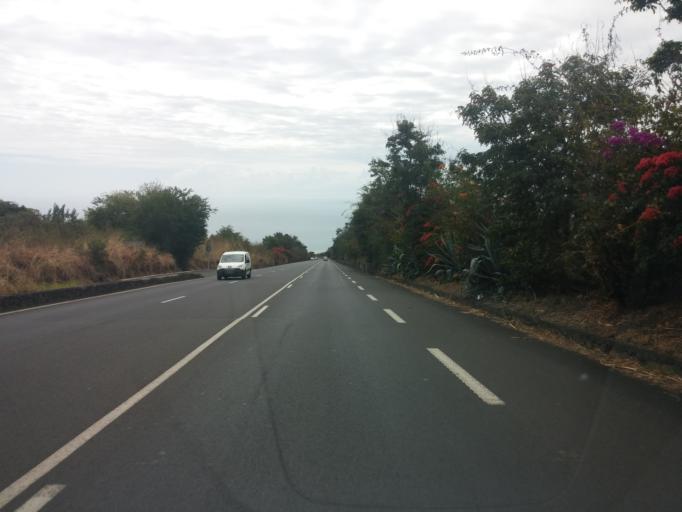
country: RE
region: Reunion
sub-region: Reunion
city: Saint-Paul
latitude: -21.0268
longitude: 55.2740
